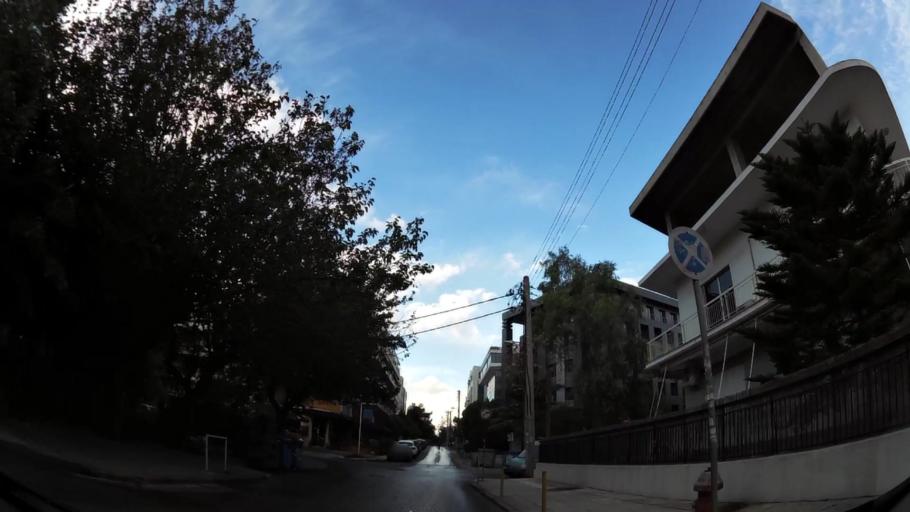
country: GR
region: Attica
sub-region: Nomarchia Athinas
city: Marousi
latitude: 38.0476
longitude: 23.8096
